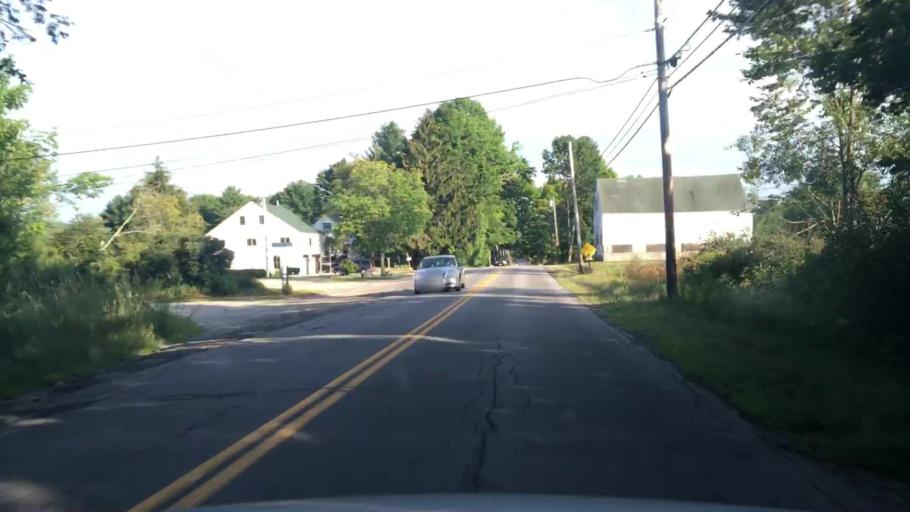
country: US
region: Maine
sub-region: Cumberland County
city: Westbrook
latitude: 43.7126
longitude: -70.3877
